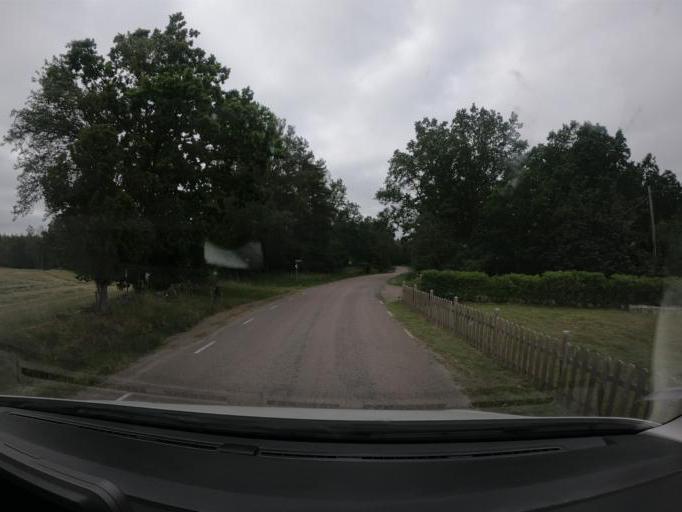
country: SE
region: Skane
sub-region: Perstorps Kommun
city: Perstorp
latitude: 56.0889
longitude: 13.3221
